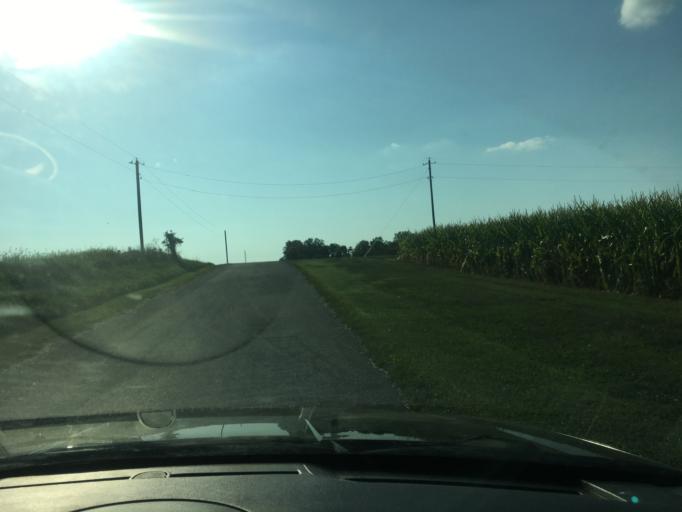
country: US
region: Ohio
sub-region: Logan County
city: West Liberty
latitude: 40.2309
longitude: -83.7888
